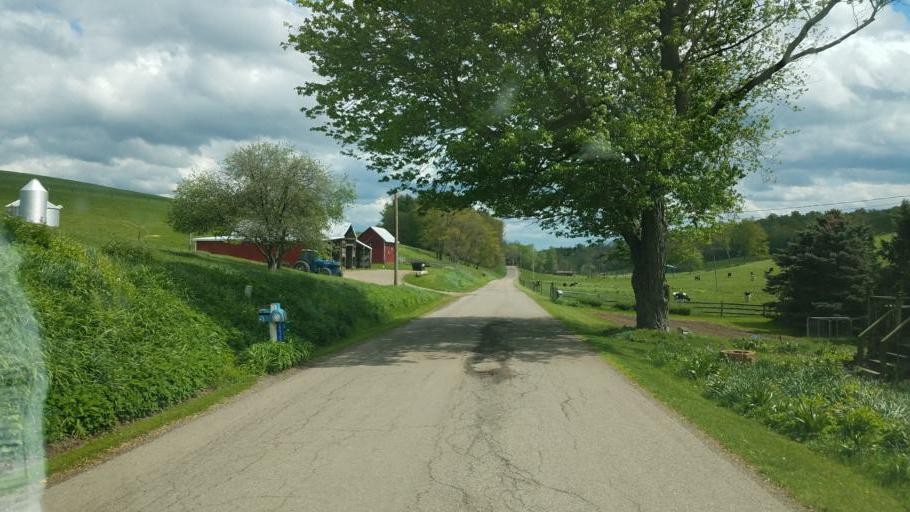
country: US
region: Ohio
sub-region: Ashland County
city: Loudonville
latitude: 40.5520
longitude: -82.2437
